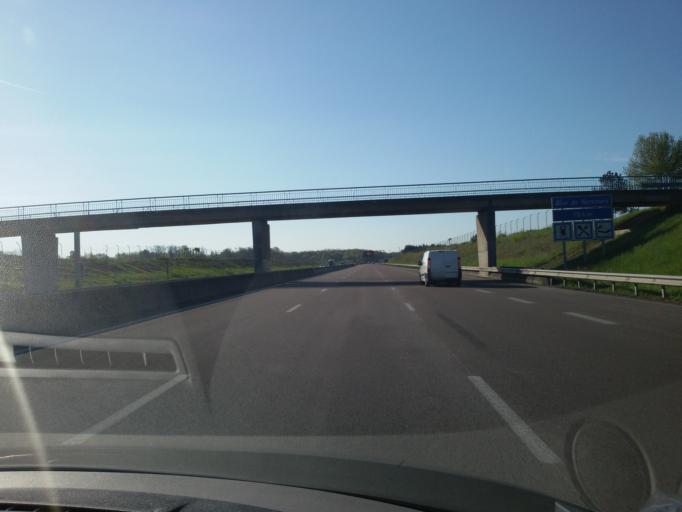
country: FR
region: Ile-de-France
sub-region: Departement de Seine-et-Marne
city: Acheres-la-Foret
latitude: 48.3601
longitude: 2.5760
